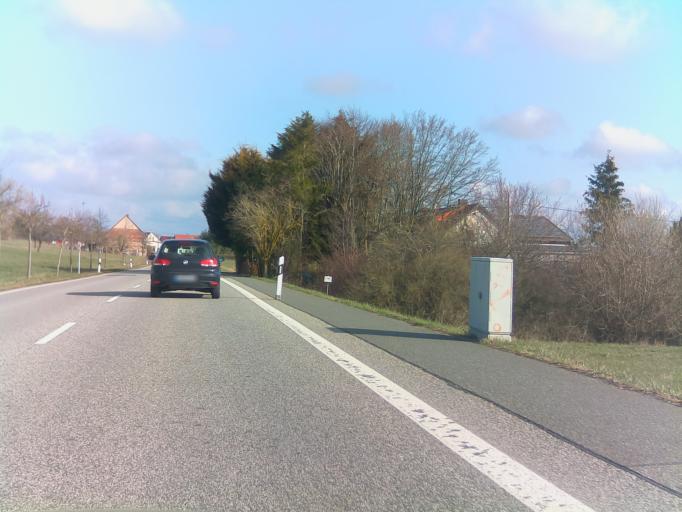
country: DE
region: Saarland
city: Blieskastel
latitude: 49.2230
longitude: 7.1833
